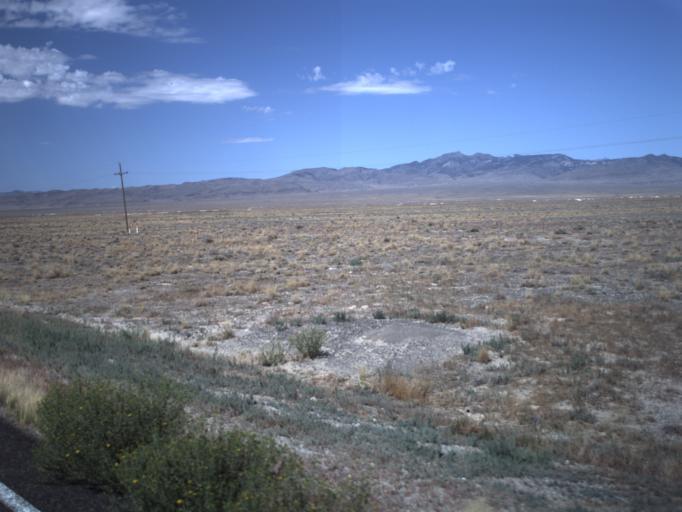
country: US
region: Utah
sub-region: Millard County
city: Delta
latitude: 39.1143
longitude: -113.1307
